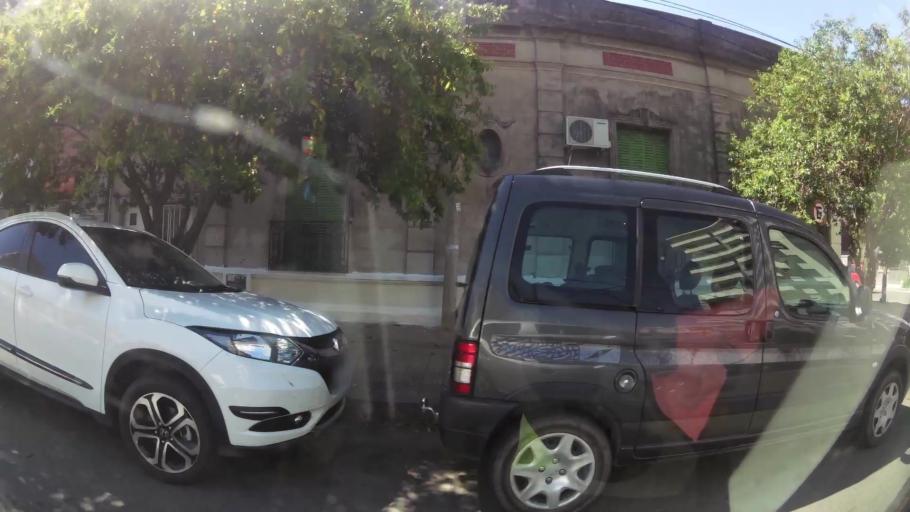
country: AR
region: Cordoba
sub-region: Departamento de Capital
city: Cordoba
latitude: -31.4172
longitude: -64.1702
